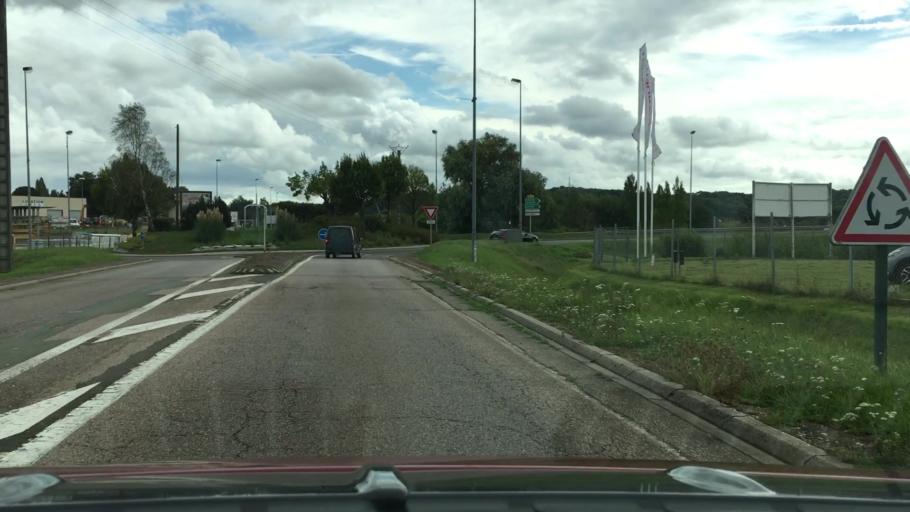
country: FR
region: Haute-Normandie
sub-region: Departement de l'Eure
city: Gisors
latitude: 49.2679
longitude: 1.7831
